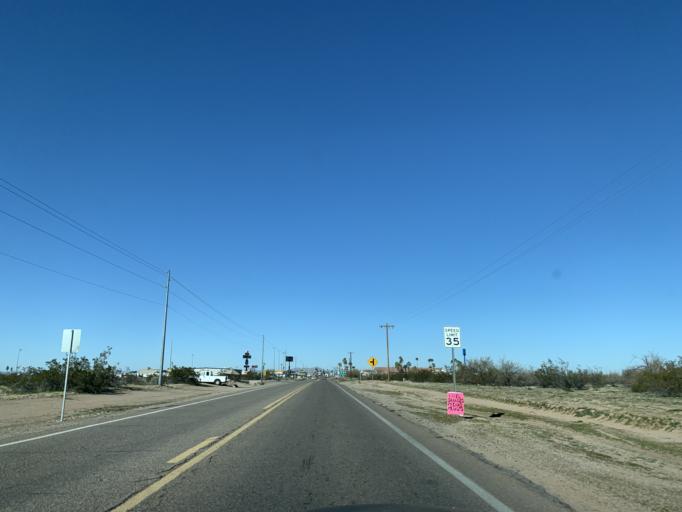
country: US
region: Arizona
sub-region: Pinal County
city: Arizona City
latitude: 32.8020
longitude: -111.6710
